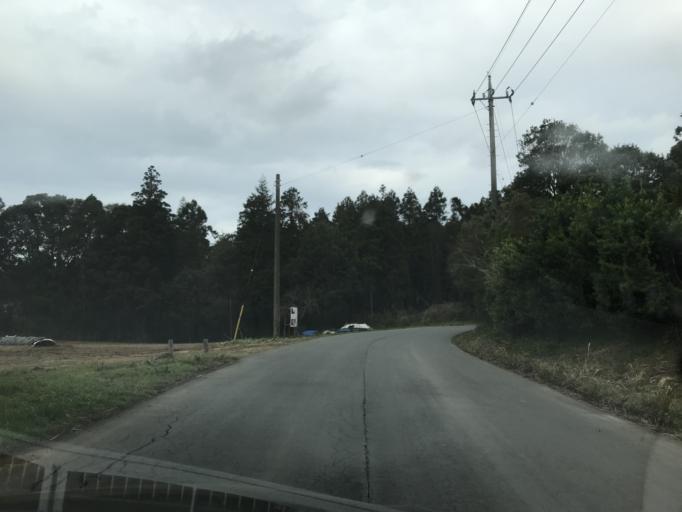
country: JP
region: Chiba
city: Sawara
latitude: 35.8538
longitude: 140.4780
